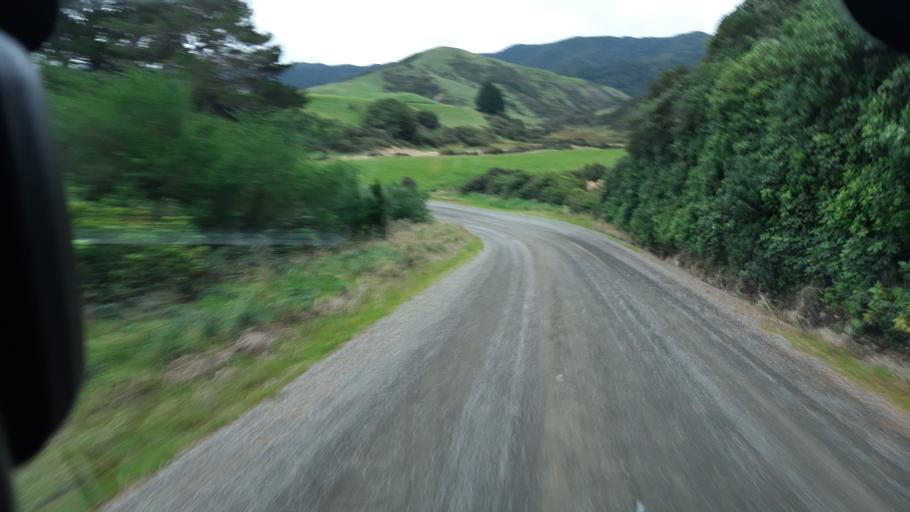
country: NZ
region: Manawatu-Wanganui
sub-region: Palmerston North City
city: Palmerston North
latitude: -40.6117
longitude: 175.6132
